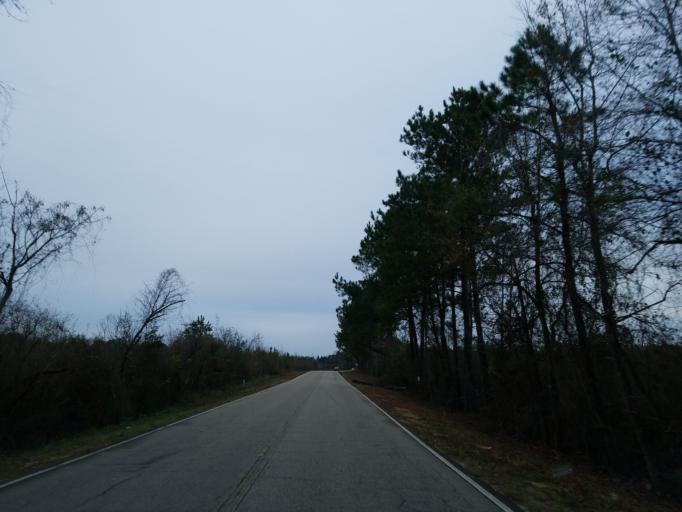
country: US
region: Mississippi
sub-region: Forrest County
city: Hattiesburg
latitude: 31.2698
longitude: -89.2424
